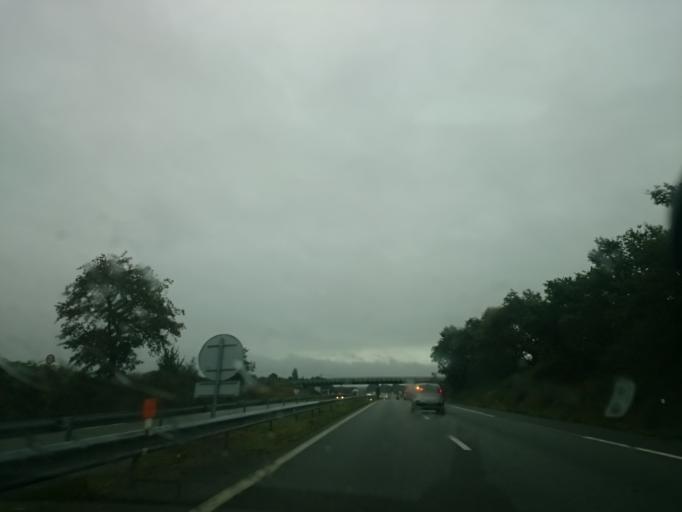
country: FR
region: Brittany
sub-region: Departement du Morbihan
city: Theix
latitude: 47.6369
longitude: -2.6695
